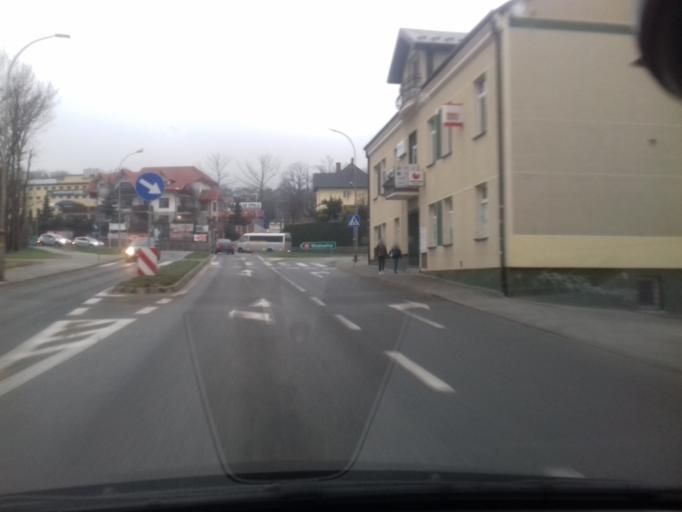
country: PL
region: Lesser Poland Voivodeship
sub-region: Powiat limanowski
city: Limanowa
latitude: 49.7093
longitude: 20.4227
